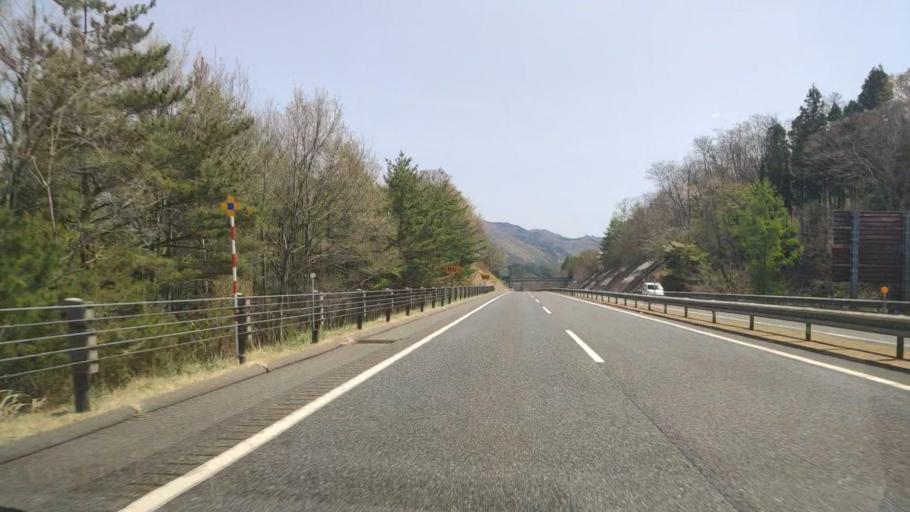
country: JP
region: Iwate
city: Ichinohe
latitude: 40.2275
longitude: 141.2748
